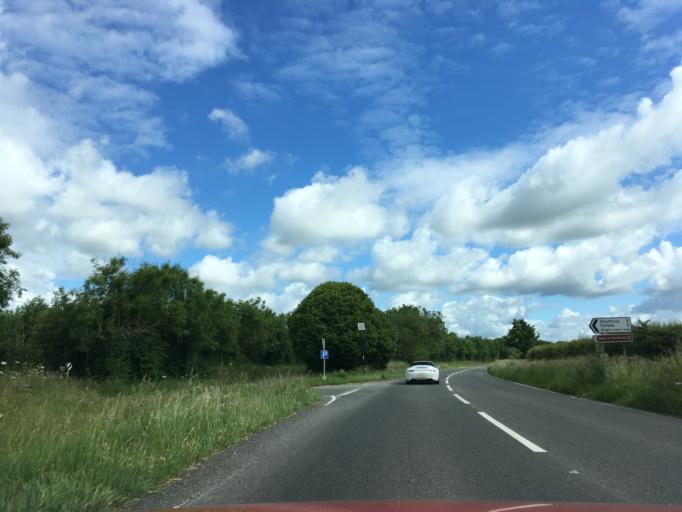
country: GB
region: England
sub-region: Gloucestershire
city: Lechlade
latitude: 51.7170
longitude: -1.6786
